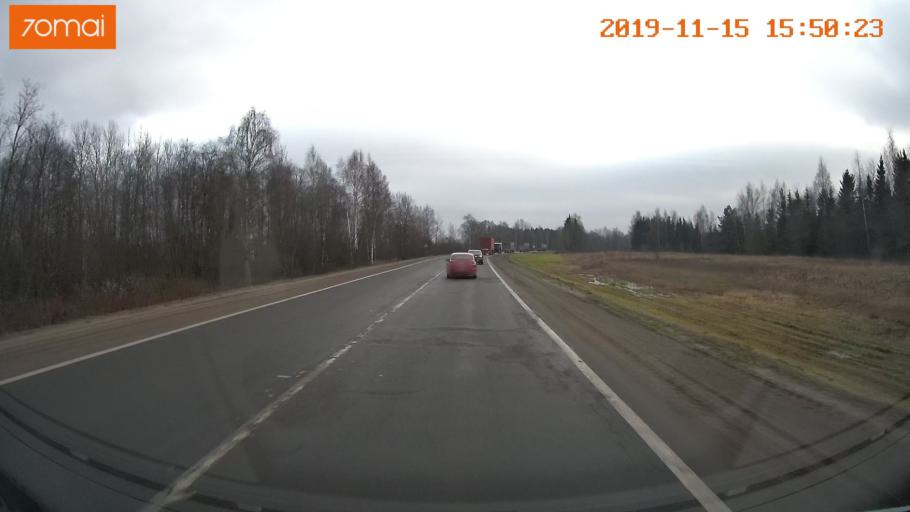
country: RU
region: Jaroslavl
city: Yaroslavl
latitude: 57.9059
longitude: 40.0133
